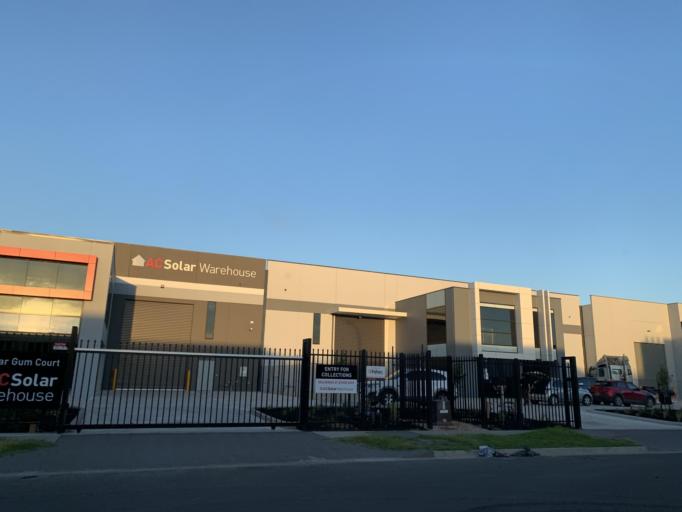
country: AU
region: Victoria
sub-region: Kingston
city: Aspendale Gardens
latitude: -38.0129
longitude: 145.1134
